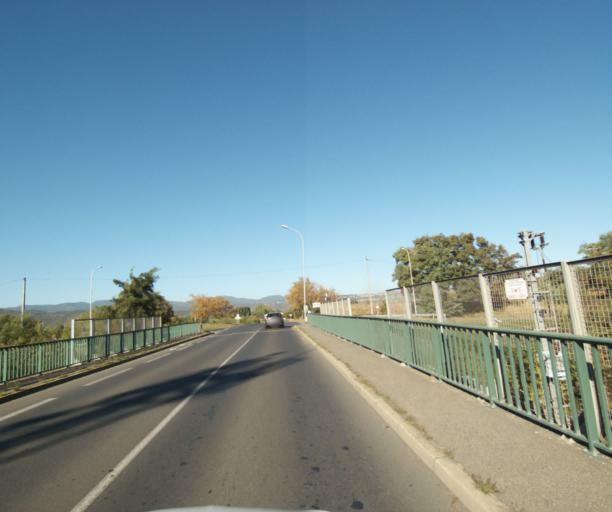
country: FR
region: Auvergne
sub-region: Departement du Puy-de-Dome
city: Gerzat
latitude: 45.8227
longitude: 3.1380
